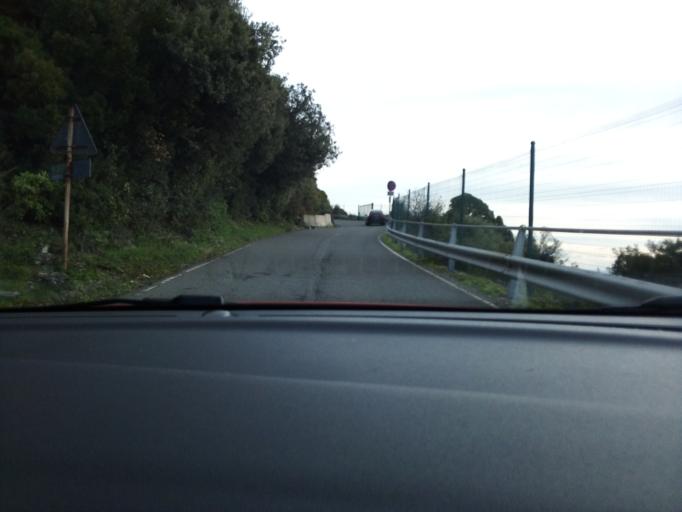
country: IT
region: Liguria
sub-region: Provincia di La Spezia
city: Riomaggiore
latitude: 44.0944
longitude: 9.7404
